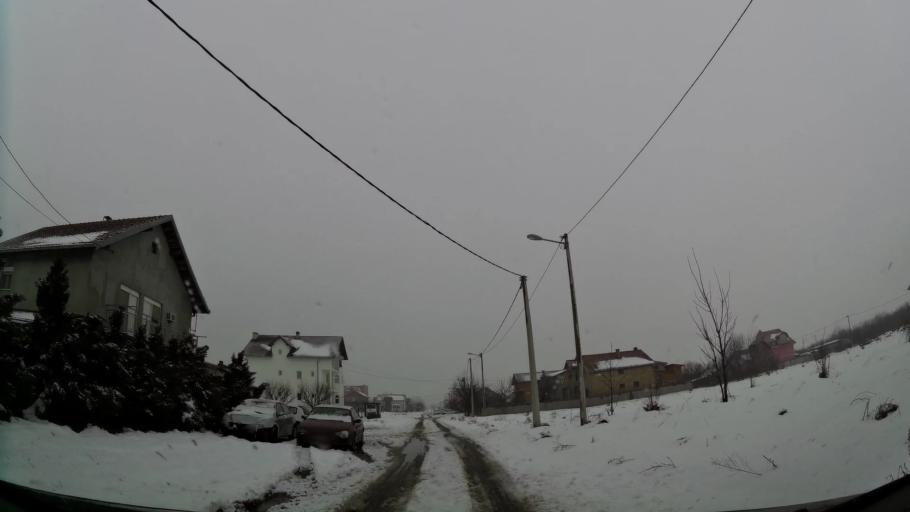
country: RS
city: Novi Banovci
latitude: 44.8744
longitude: 20.3126
